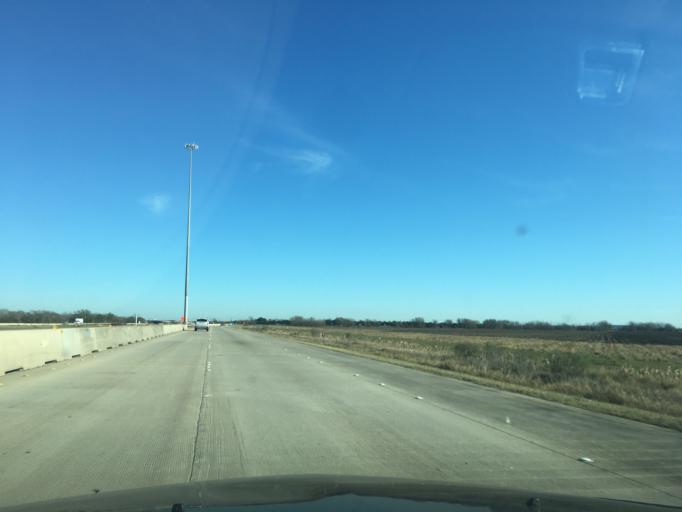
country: US
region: Texas
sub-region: Fort Bend County
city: Rosenberg
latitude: 29.5325
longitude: -95.8330
